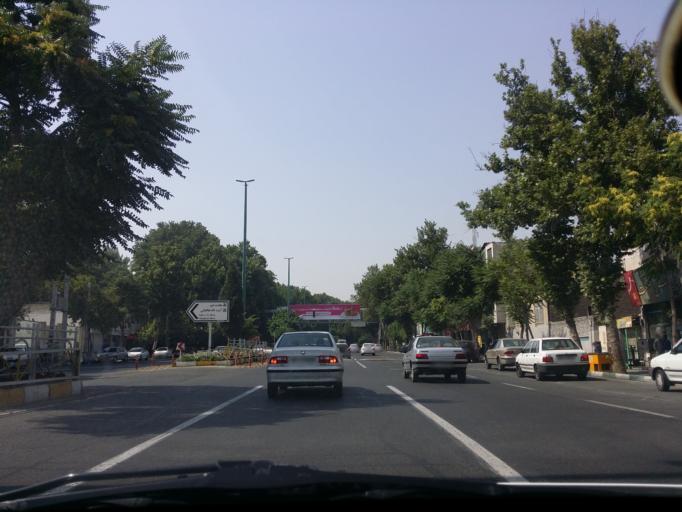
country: IR
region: Alborz
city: Karaj
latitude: 35.8009
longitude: 51.0013
